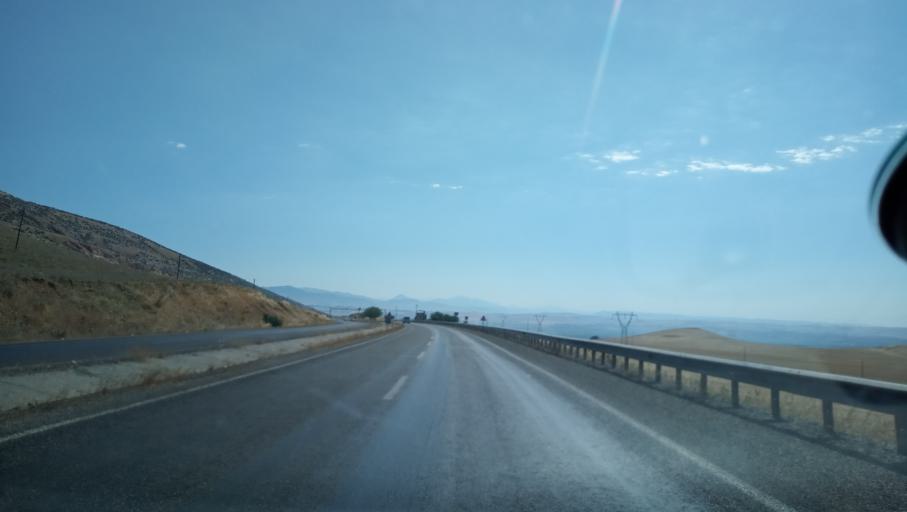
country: TR
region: Diyarbakir
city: Malabadi
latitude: 38.1185
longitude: 41.1438
